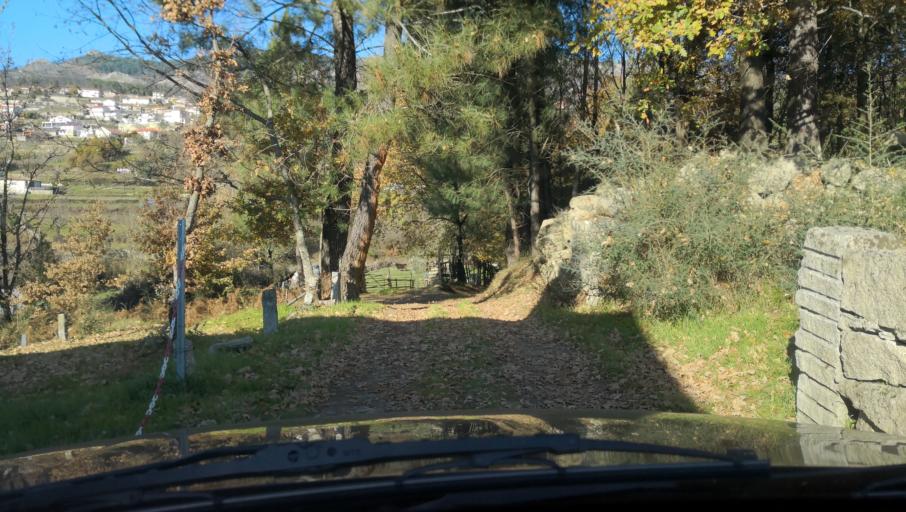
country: PT
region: Vila Real
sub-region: Vila Real
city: Vila Real
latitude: 41.3287
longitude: -7.7434
